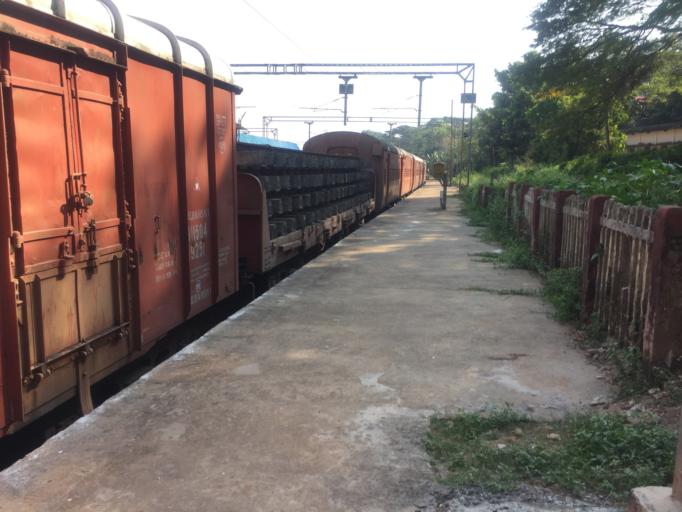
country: IN
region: Karnataka
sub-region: Dakshina Kannada
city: Ullal
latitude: 12.8620
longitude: 74.8431
